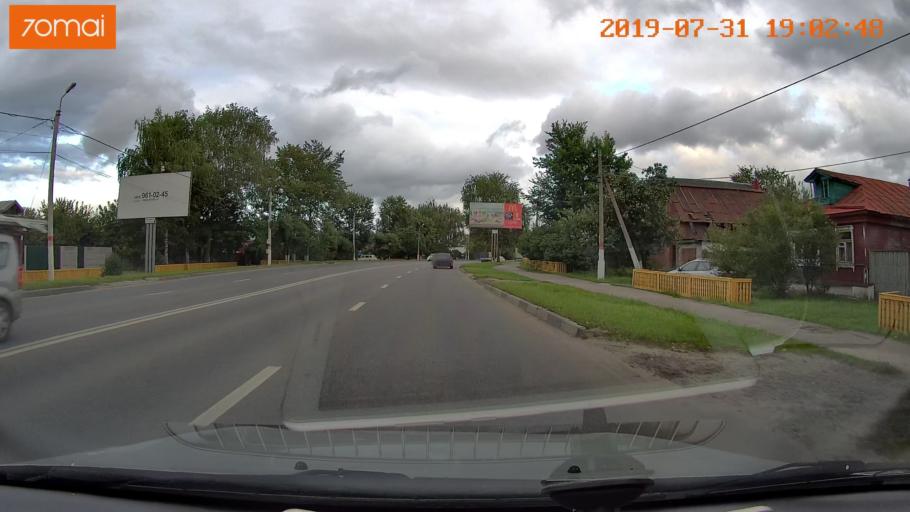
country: RU
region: Moskovskaya
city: Raduzhnyy
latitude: 55.1187
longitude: 38.7346
